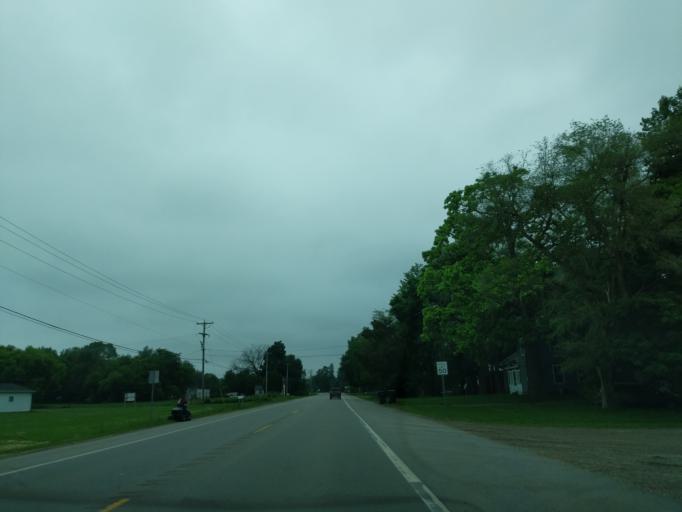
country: US
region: Michigan
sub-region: Branch County
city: Quincy
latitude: 41.9484
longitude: -84.8664
